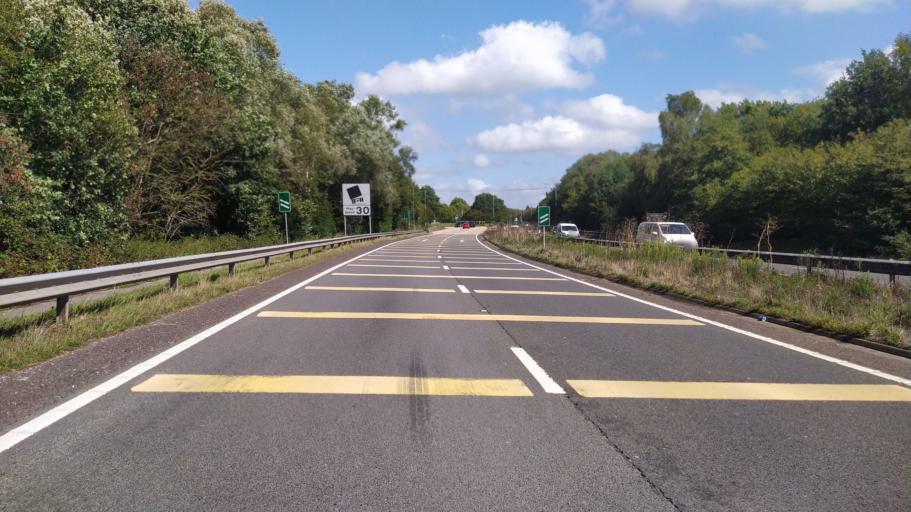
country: GB
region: England
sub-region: Hampshire
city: Liss
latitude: 51.0576
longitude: -0.9019
